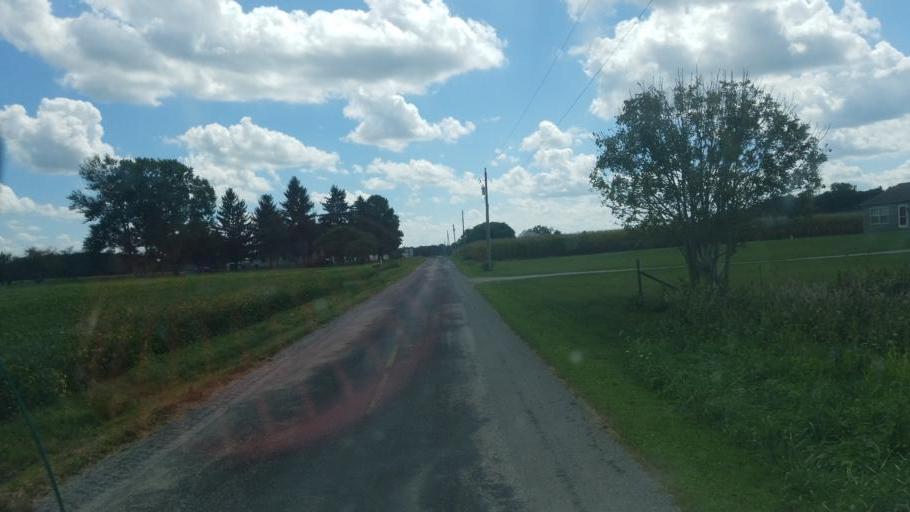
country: US
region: Ohio
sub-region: Marion County
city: Prospect
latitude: 40.4646
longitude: -83.1680
